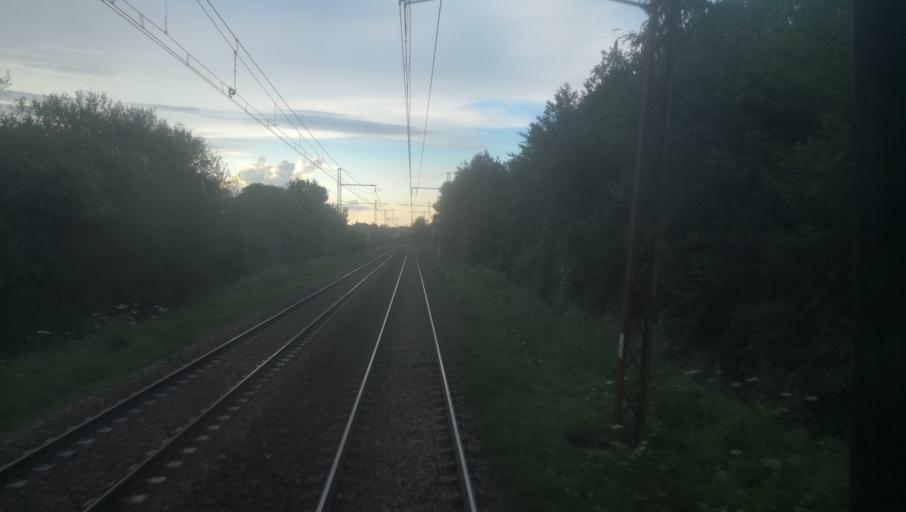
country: FR
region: Limousin
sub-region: Departement de la Creuse
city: La Souterraine
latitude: 46.2322
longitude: 1.4964
